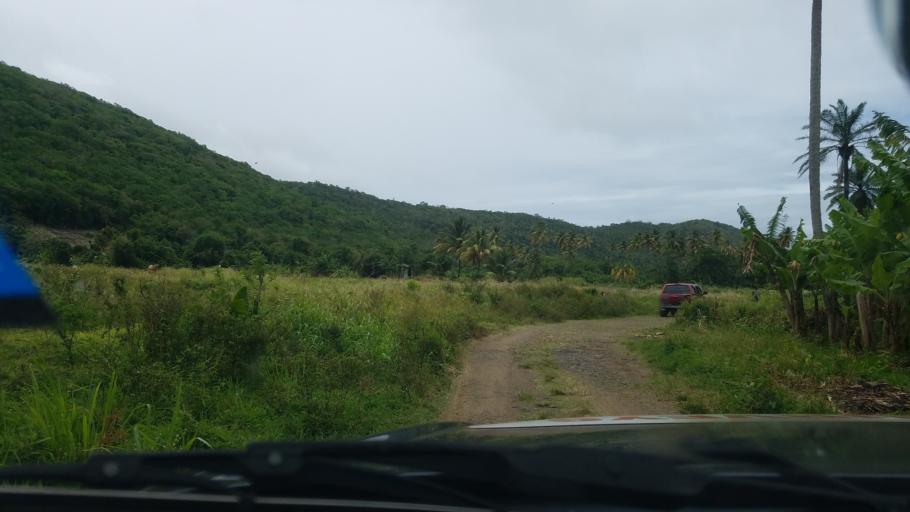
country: LC
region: Gros-Islet
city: Gros Islet
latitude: 14.0268
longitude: -60.9109
